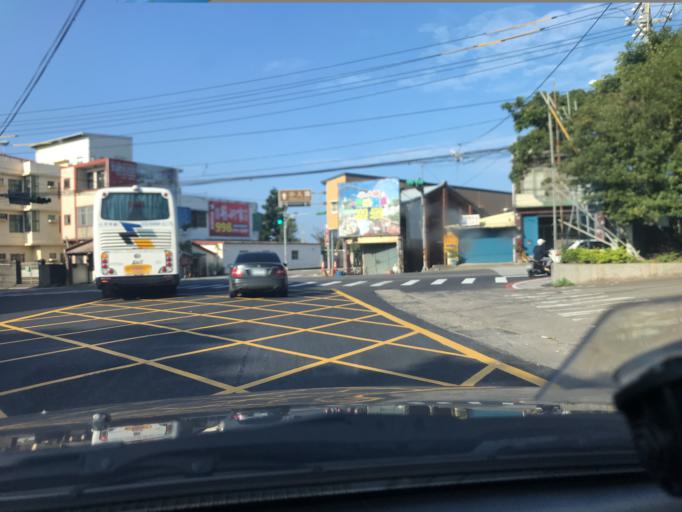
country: TW
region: Taiwan
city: Daxi
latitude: 24.8299
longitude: 121.1931
